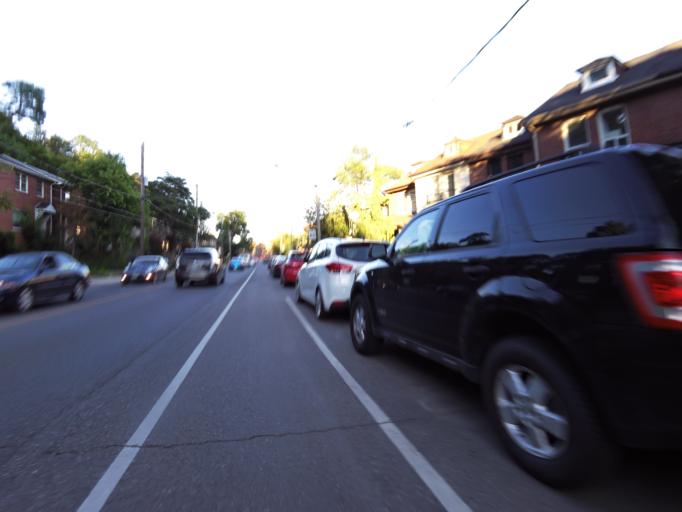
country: CA
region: Ontario
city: Toronto
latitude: 43.6768
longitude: -79.4131
